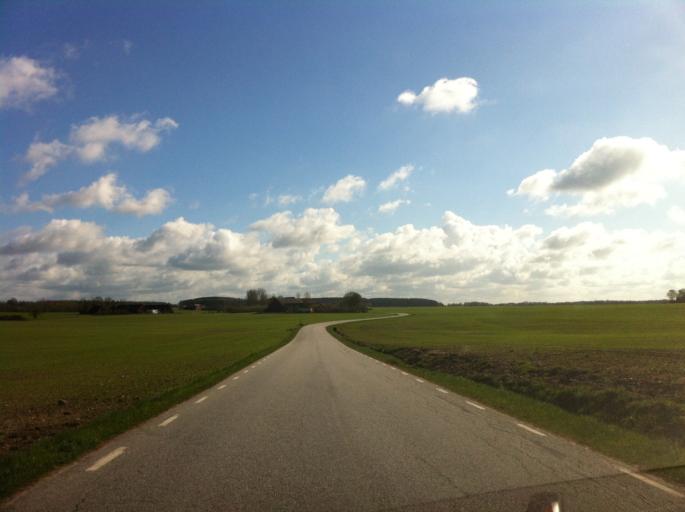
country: SE
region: Skane
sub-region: Eslovs Kommun
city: Eslov
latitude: 55.8653
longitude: 13.2399
